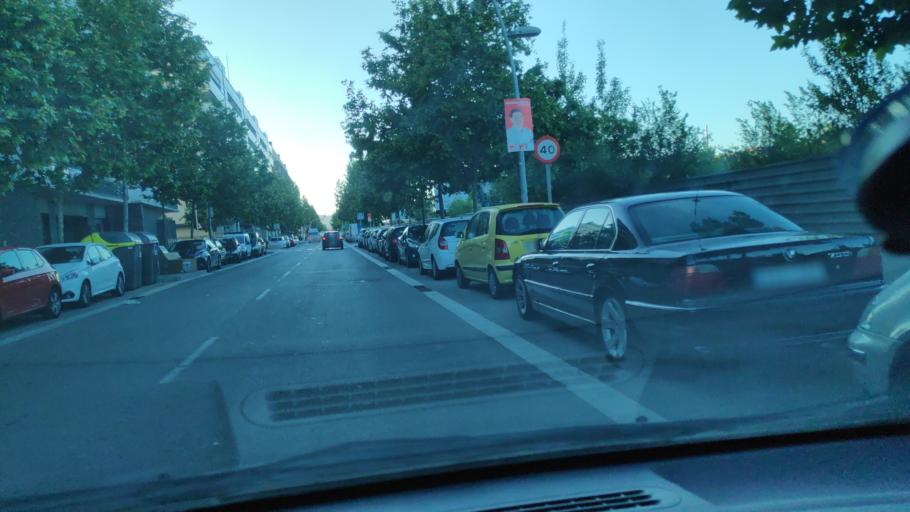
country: ES
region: Catalonia
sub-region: Provincia de Barcelona
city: Sant Adria de Besos
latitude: 41.4235
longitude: 2.2220
